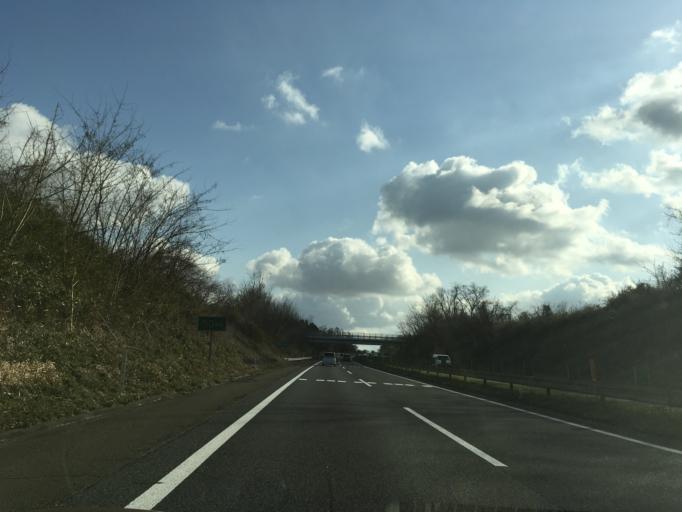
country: JP
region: Miyagi
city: Furukawa
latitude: 38.6704
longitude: 140.9806
